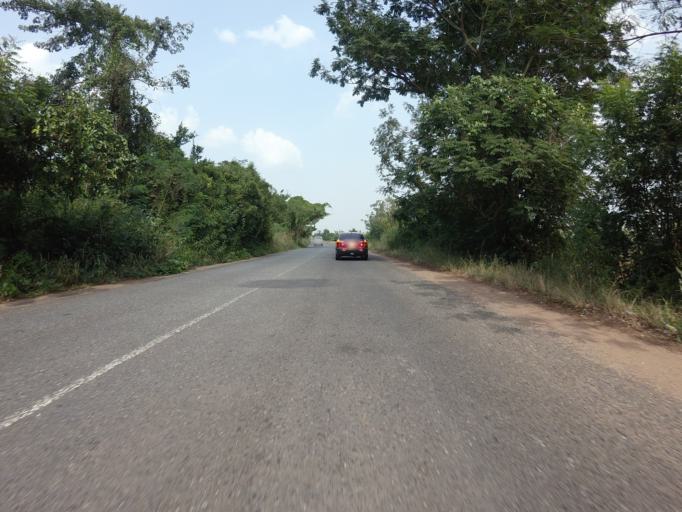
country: GH
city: Akropong
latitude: 5.9395
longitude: -0.0264
